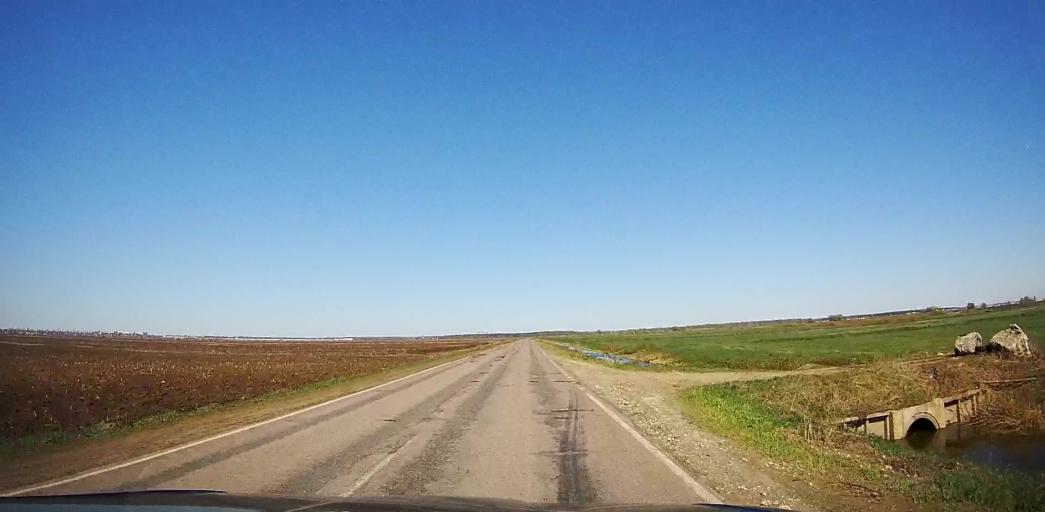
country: RU
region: Moskovskaya
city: Ramenskoye
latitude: 55.5057
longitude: 38.2508
